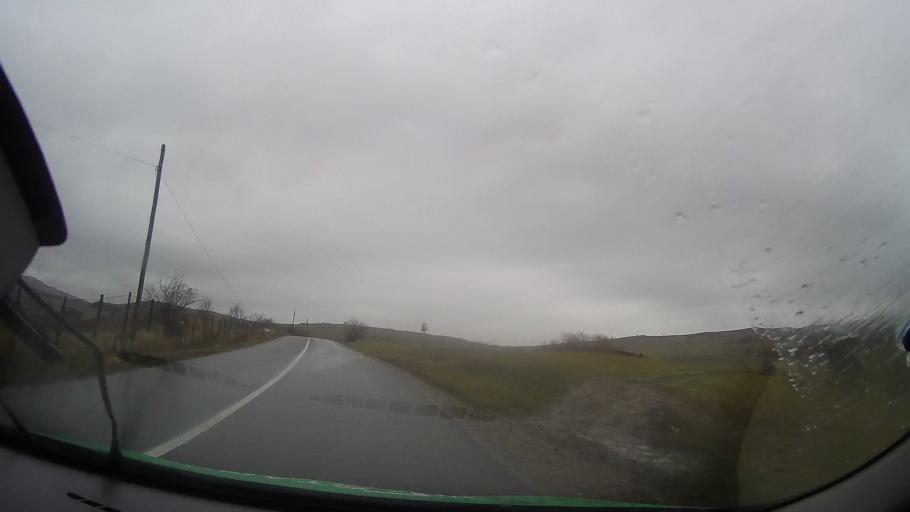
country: RO
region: Bistrita-Nasaud
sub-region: Comuna Monor
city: Monor
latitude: 46.9537
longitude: 24.6800
